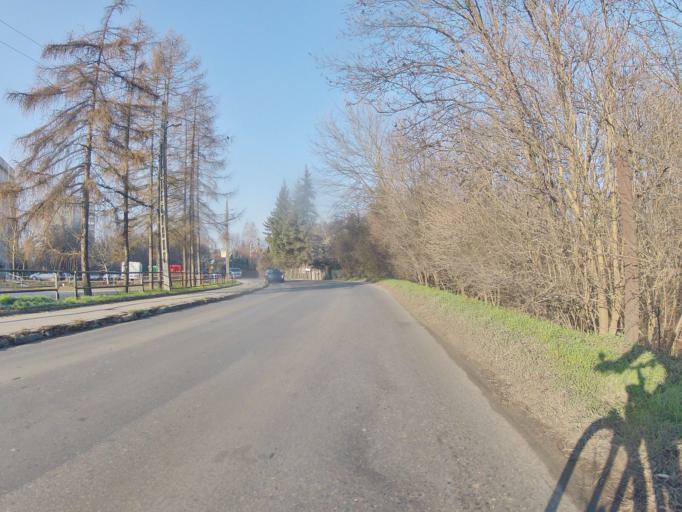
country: PL
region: Lesser Poland Voivodeship
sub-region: Krakow
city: Krakow
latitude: 50.0877
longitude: 19.9461
